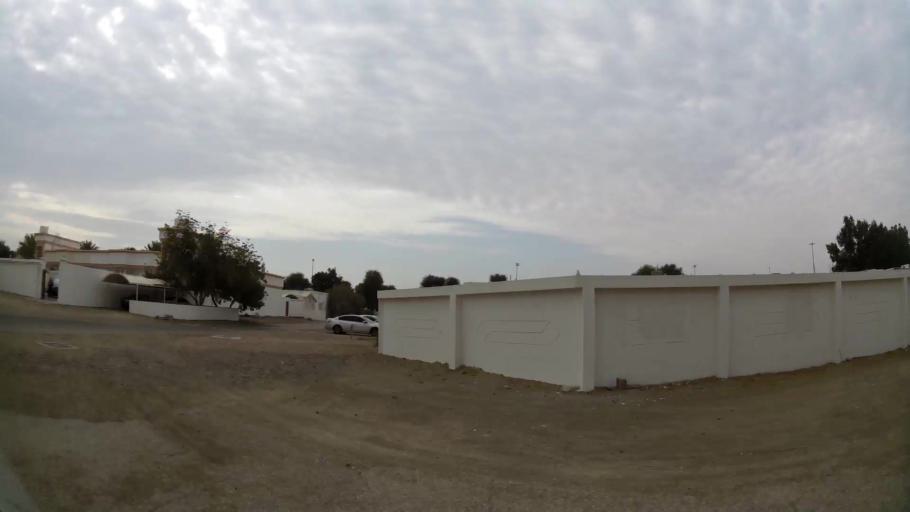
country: AE
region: Abu Dhabi
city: Al Ain
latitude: 24.2259
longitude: 55.7423
